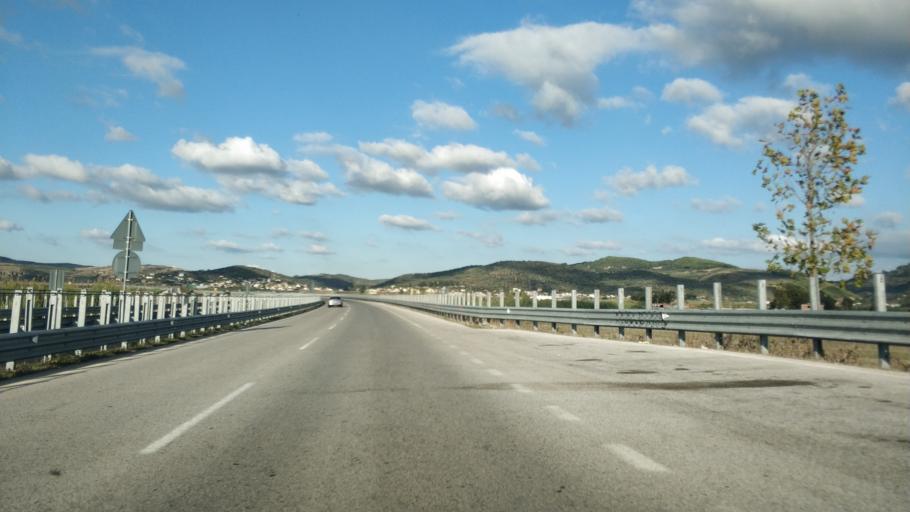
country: AL
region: Fier
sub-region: Rrethi i Fierit
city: Levan
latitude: 40.6607
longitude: 19.4727
